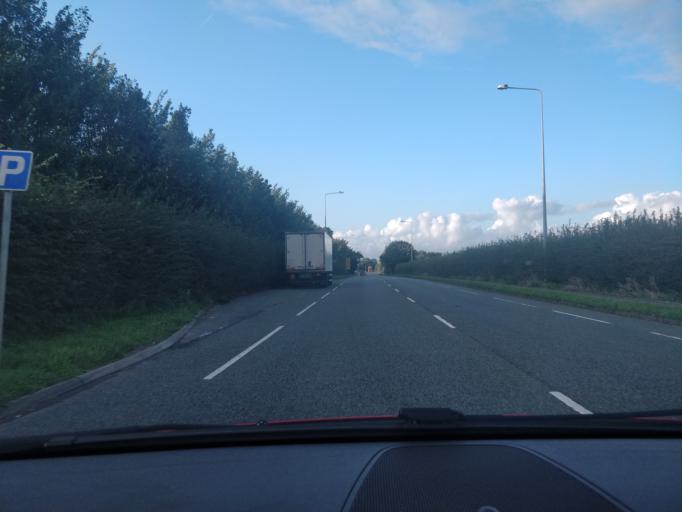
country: GB
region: England
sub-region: Lancashire
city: Tarleton
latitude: 53.6923
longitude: -2.8143
